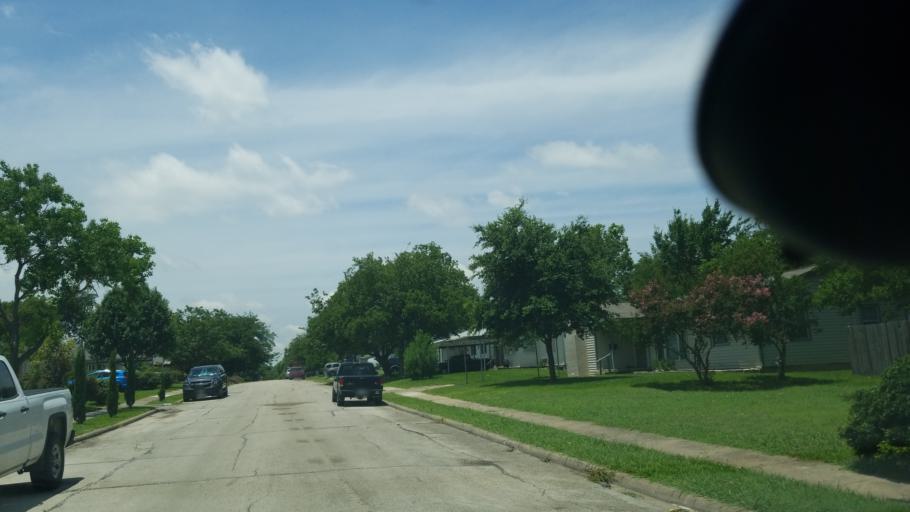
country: US
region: Texas
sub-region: Dallas County
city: Irving
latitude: 32.8456
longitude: -96.9726
